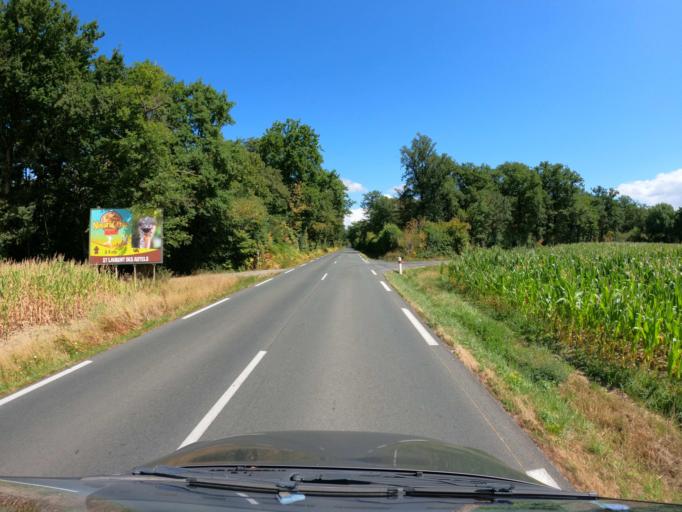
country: FR
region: Pays de la Loire
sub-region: Departement de Maine-et-Loire
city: Saint-Laurent-des-Autels
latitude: 47.2629
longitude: -1.2018
